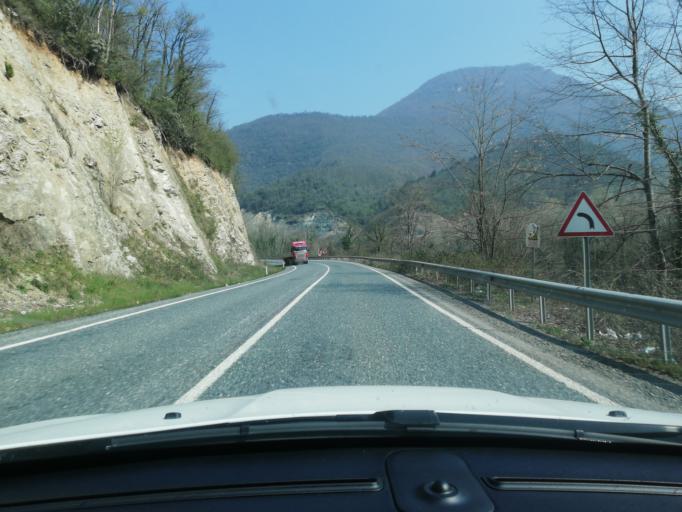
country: TR
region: Zonguldak
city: Gokcebey
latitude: 41.2517
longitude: 32.1633
